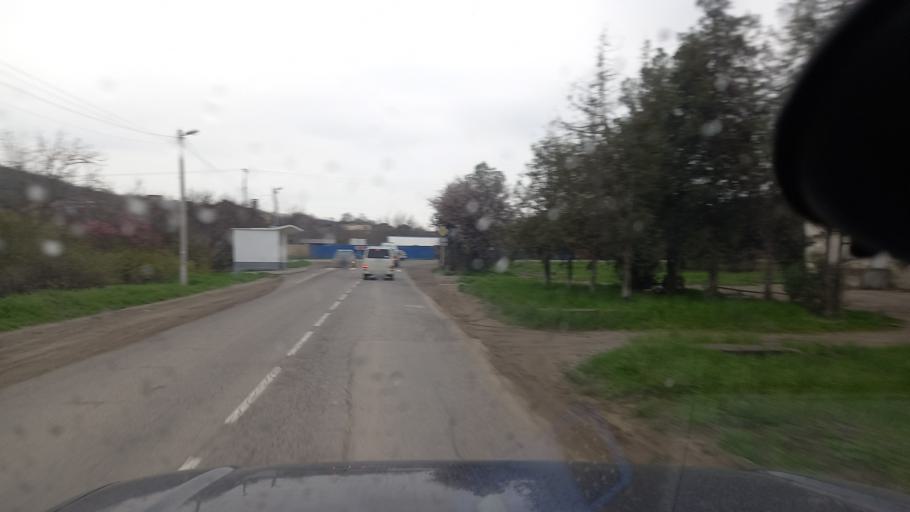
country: RU
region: Krasnodarskiy
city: Sukko
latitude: 44.8609
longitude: 37.4398
